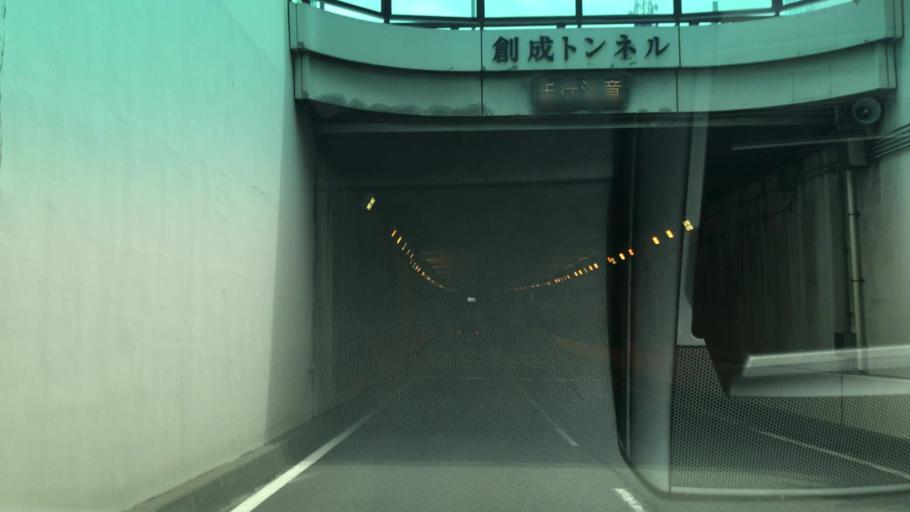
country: JP
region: Hokkaido
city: Sapporo
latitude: 43.0640
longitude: 141.3564
